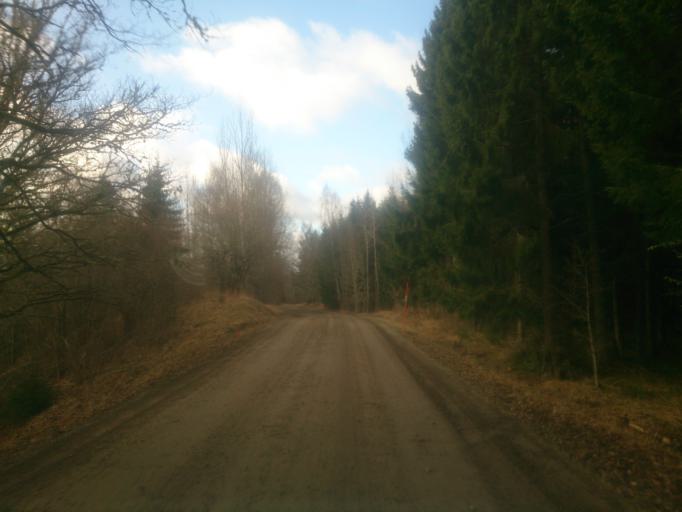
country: SE
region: OEstergoetland
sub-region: Atvidabergs Kommun
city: Atvidaberg
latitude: 58.1901
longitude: 16.1473
